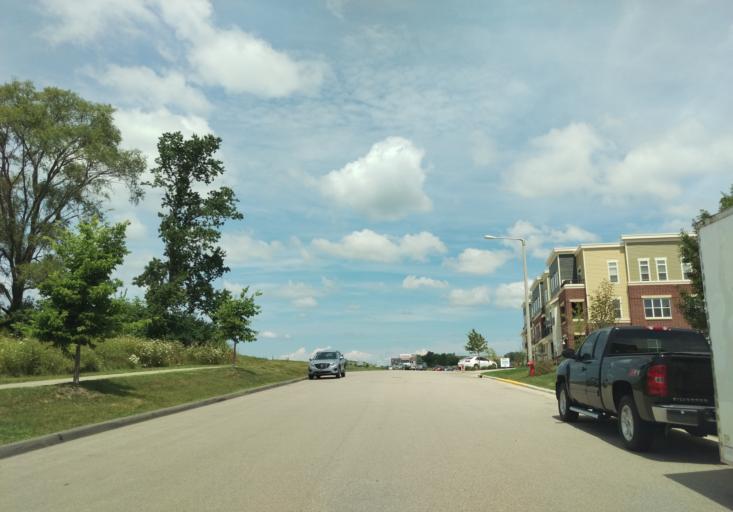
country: US
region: Wisconsin
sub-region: Dane County
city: Middleton
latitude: 43.1147
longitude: -89.5146
